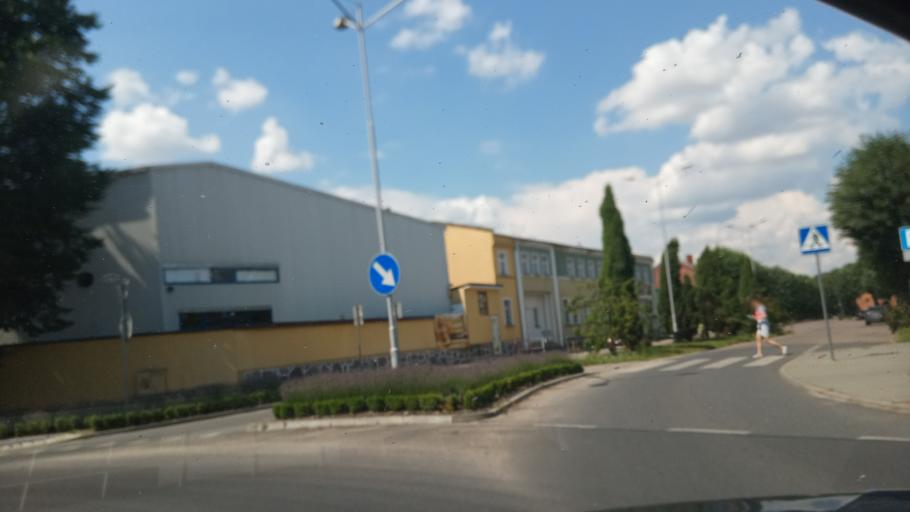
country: PL
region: West Pomeranian Voivodeship
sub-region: Powiat swidwinski
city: Polczyn-Zdroj
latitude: 53.7642
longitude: 16.0995
